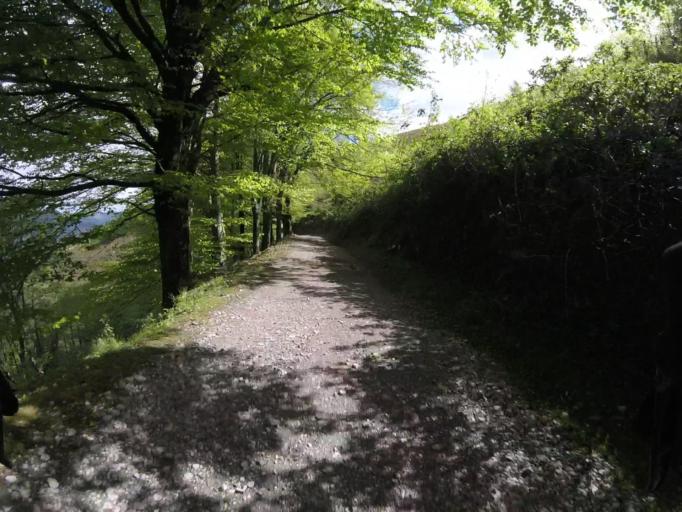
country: ES
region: Navarre
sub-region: Provincia de Navarra
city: Arano
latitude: 43.1805
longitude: -1.9017
